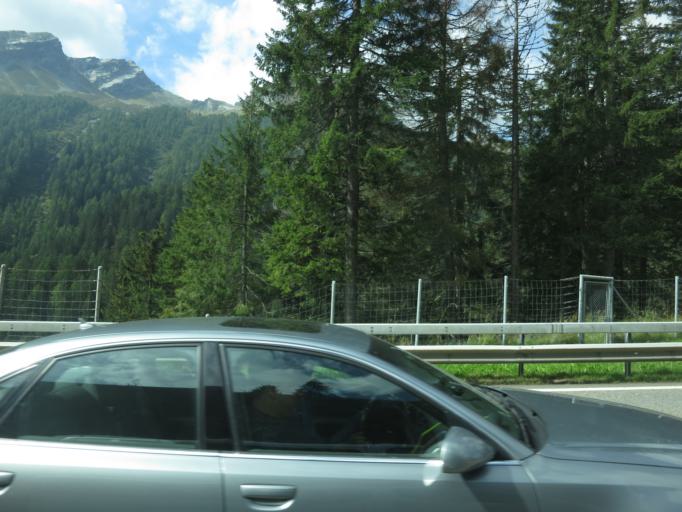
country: CH
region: Grisons
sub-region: Moesa District
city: Mesocco
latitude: 46.4389
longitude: 9.1928
